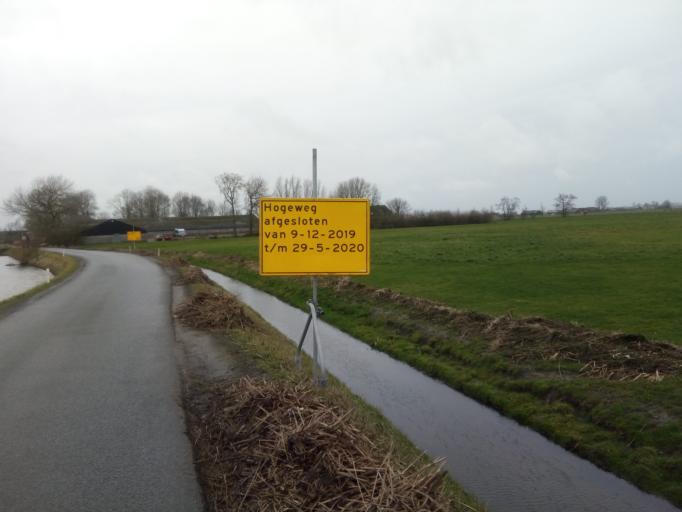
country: NL
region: Groningen
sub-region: Gemeente Zuidhorn
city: Aduard
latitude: 53.2310
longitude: 6.4615
